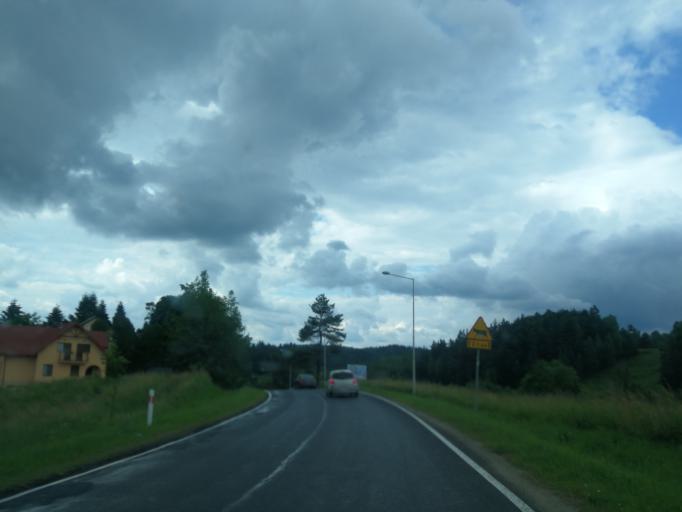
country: PL
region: Subcarpathian Voivodeship
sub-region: Powiat leski
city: Olszanica
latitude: 49.4396
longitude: 22.4540
